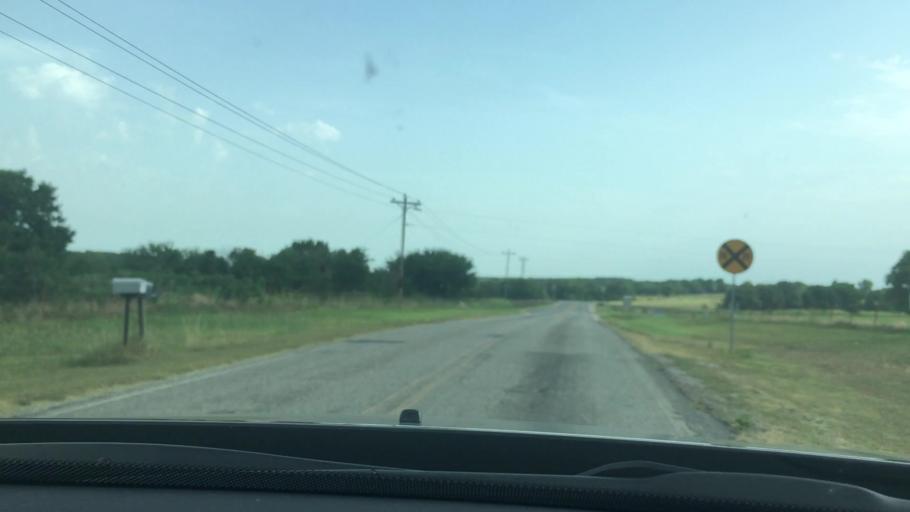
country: US
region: Oklahoma
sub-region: Pontotoc County
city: Byng
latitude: 34.8482
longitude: -96.6170
